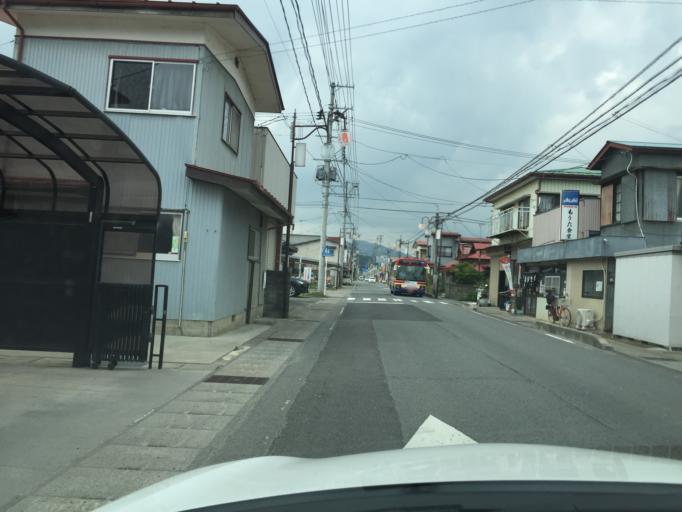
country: JP
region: Fukushima
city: Funehikimachi-funehiki
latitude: 37.2772
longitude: 140.6345
